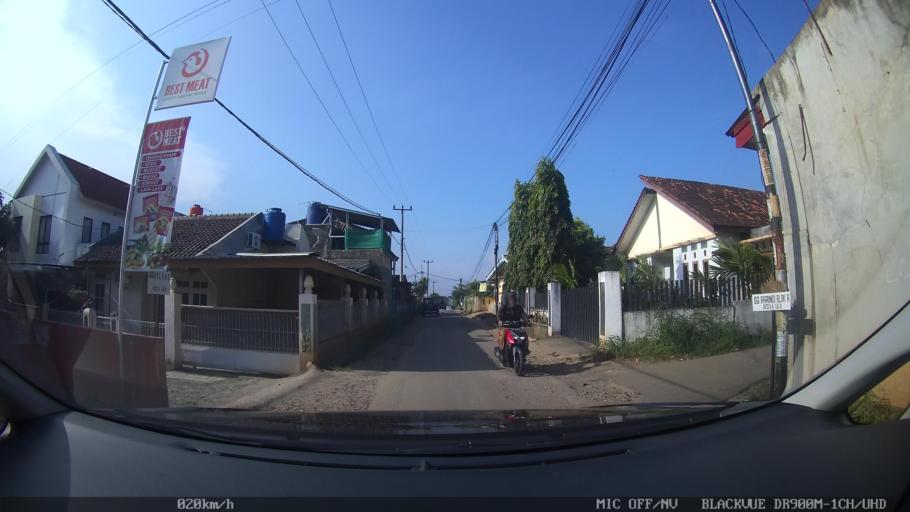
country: ID
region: Lampung
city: Kedaton
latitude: -5.3704
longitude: 105.2332
